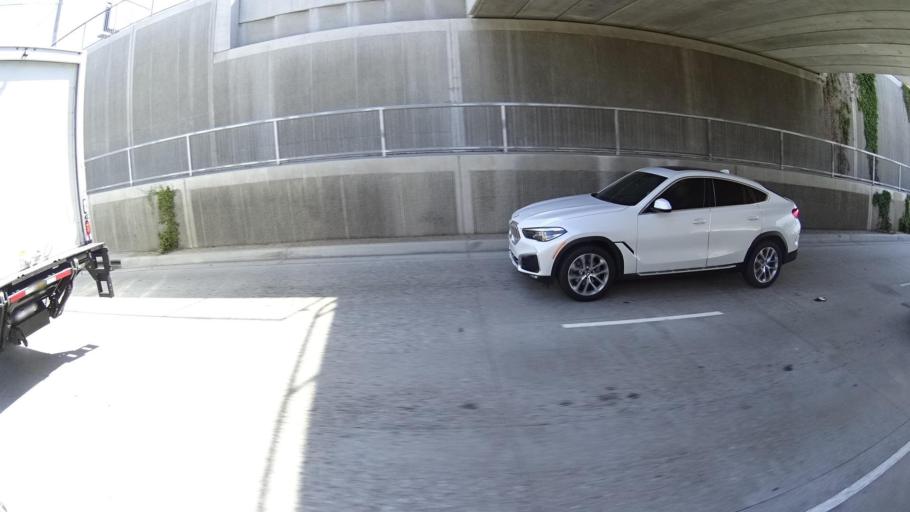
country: US
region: California
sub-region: Los Angeles County
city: South San Jose Hills
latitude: 33.9976
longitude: -117.8883
